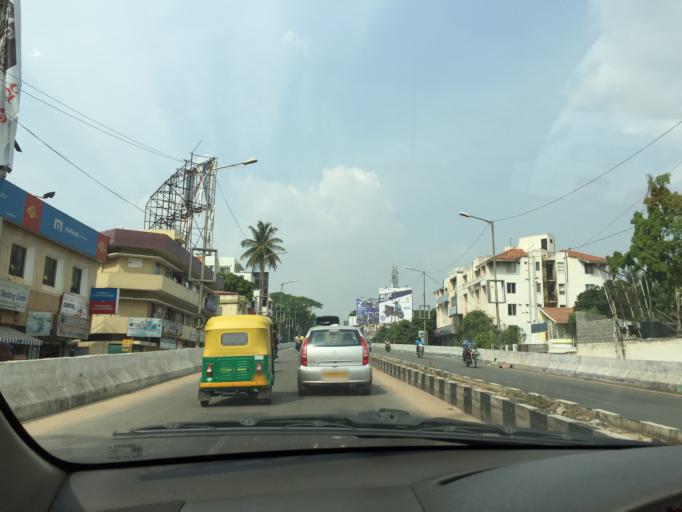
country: IN
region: Karnataka
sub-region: Bangalore Urban
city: Bangalore
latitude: 12.9964
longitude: 77.6180
